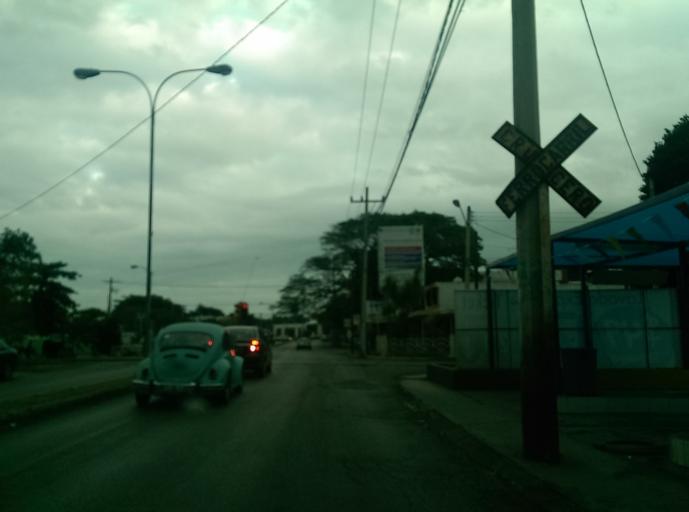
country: MX
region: Yucatan
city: Merida
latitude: 20.9889
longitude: -89.6415
